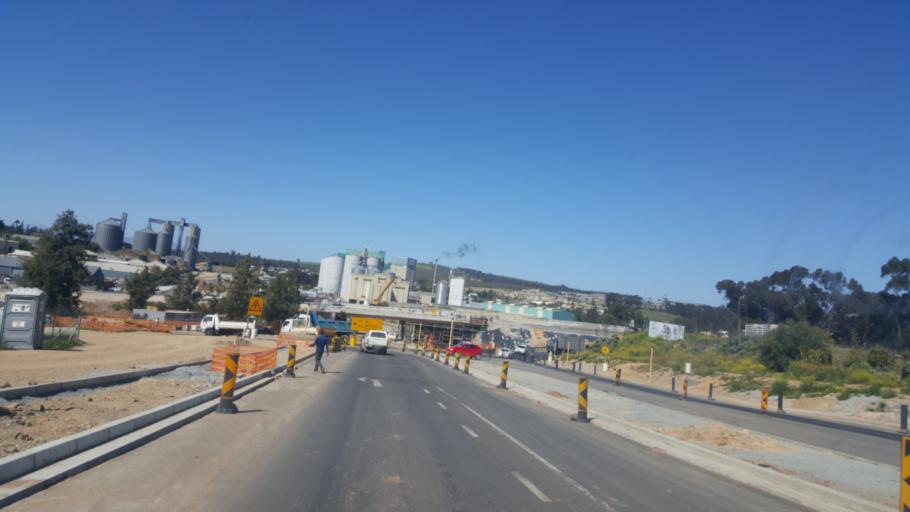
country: ZA
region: Western Cape
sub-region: West Coast District Municipality
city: Malmesbury
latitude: -33.4646
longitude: 18.7157
